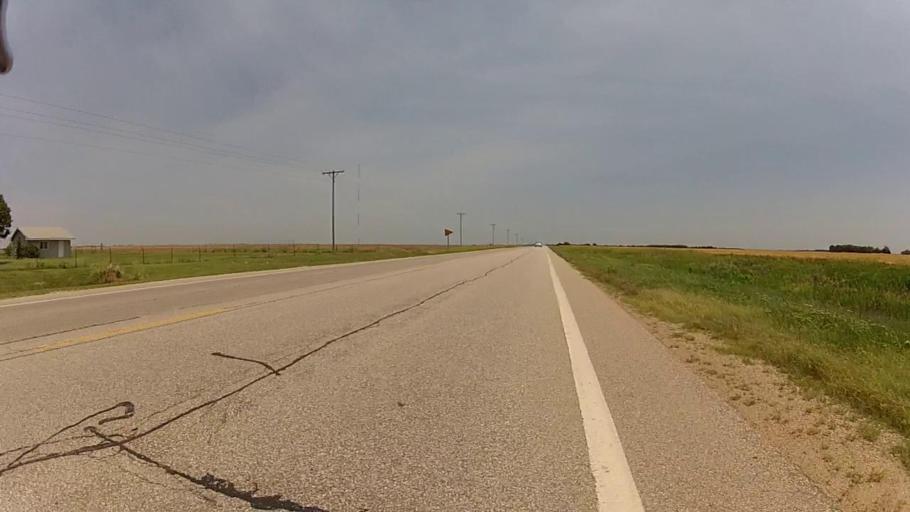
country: US
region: Kansas
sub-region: Cowley County
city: Arkansas City
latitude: 37.0565
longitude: -97.1037
